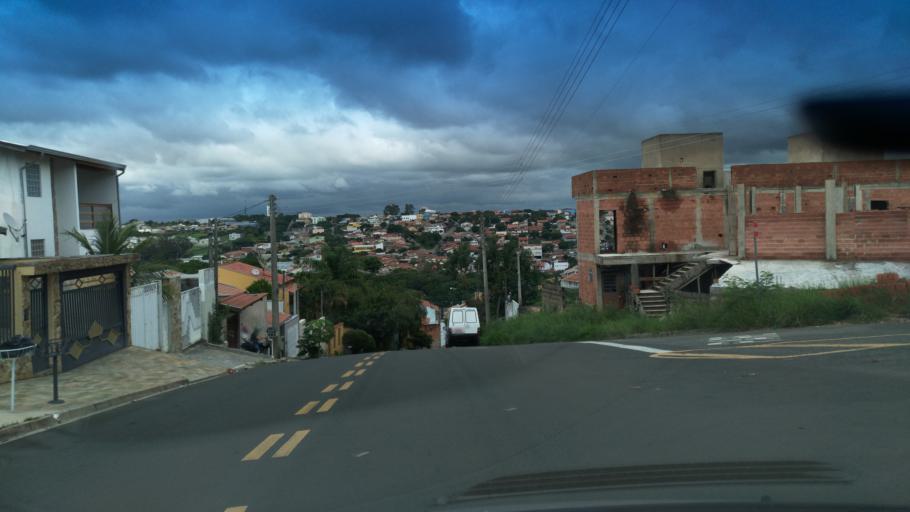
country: BR
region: Sao Paulo
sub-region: Valinhos
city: Valinhos
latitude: -22.9581
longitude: -46.9750
